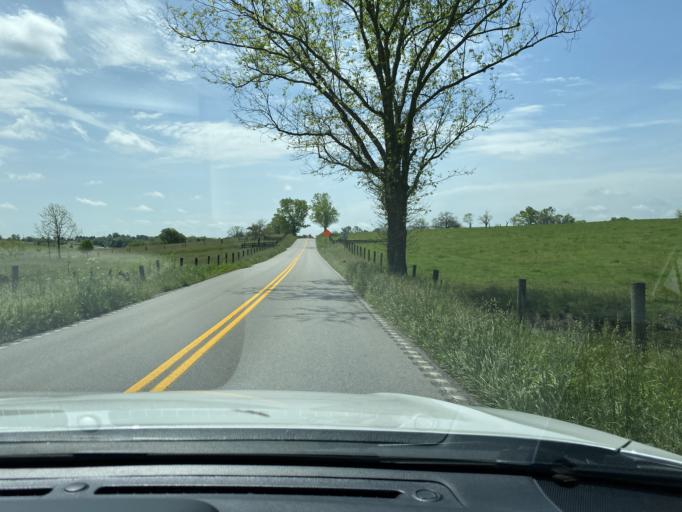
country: US
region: Kentucky
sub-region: Scott County
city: Georgetown
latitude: 38.2483
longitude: -84.5879
